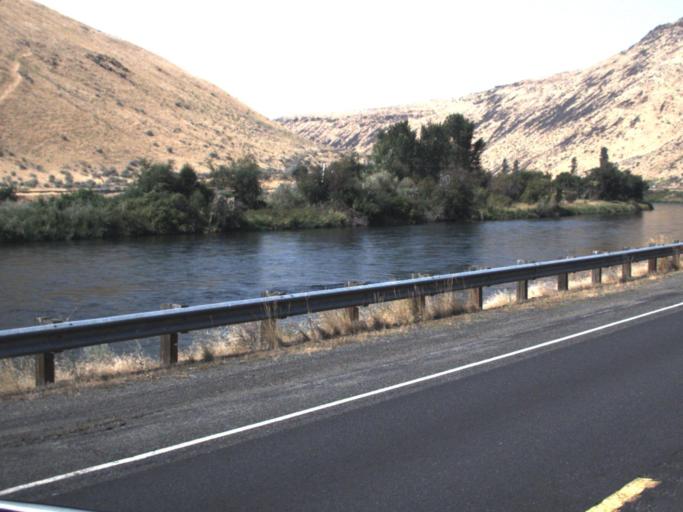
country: US
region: Washington
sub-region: Kittitas County
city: Kittitas
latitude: 46.8624
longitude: -120.4788
